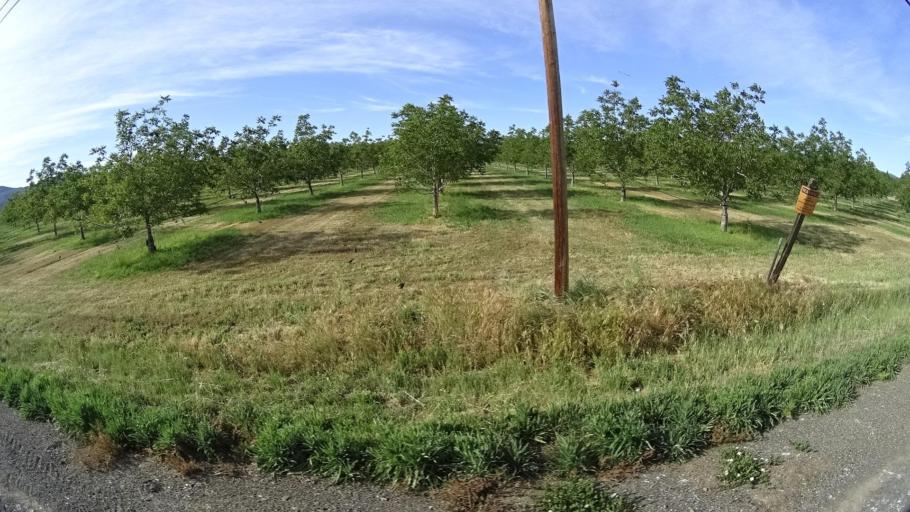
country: US
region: California
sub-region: Lake County
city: Kelseyville
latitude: 38.9893
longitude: -122.8491
